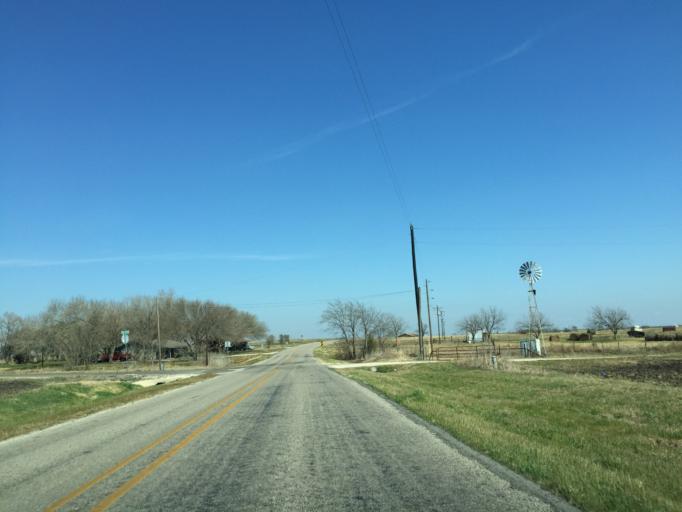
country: US
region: Texas
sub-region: Williamson County
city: Granger
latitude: 30.7484
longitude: -97.5572
